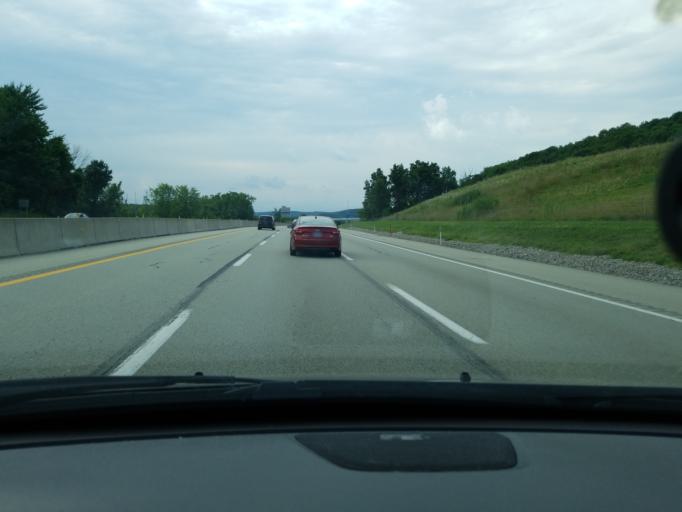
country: US
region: Pennsylvania
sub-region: Lawrence County
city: New Beaver
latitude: 40.8480
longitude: -80.3935
